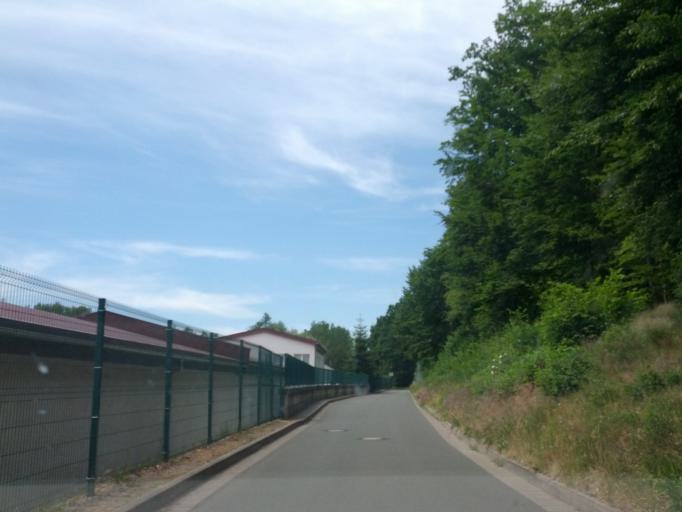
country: DE
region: Thuringia
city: Seebach
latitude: 50.9559
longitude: 10.4057
